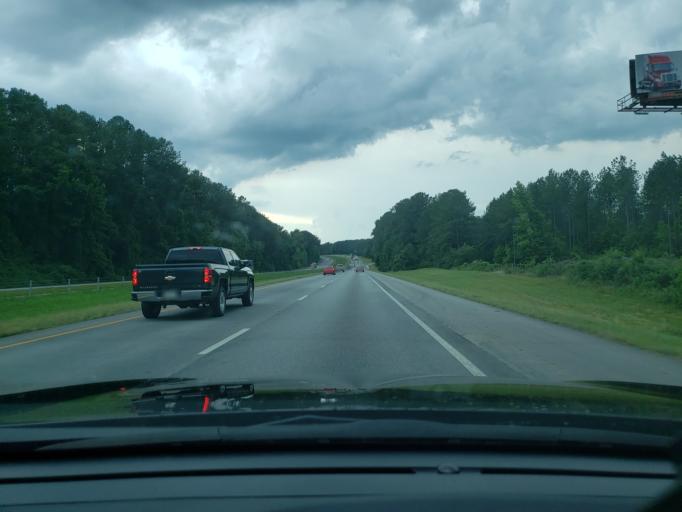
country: US
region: Georgia
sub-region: Troup County
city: La Grange
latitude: 32.9530
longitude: -85.0929
